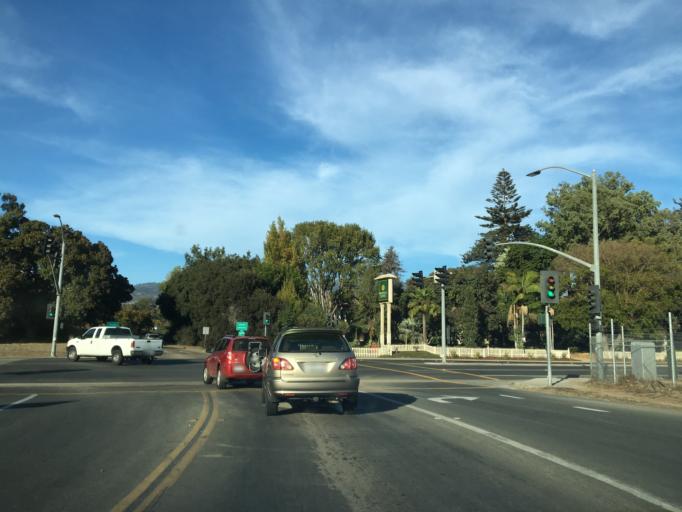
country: US
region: California
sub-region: Santa Barbara County
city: Goleta
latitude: 34.4350
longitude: -119.8169
